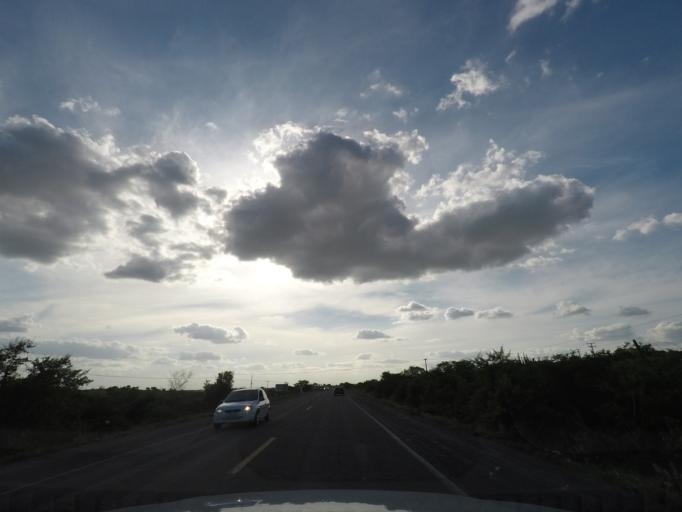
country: BR
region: Bahia
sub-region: Anguera
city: Anguera
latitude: -12.1855
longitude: -39.4797
